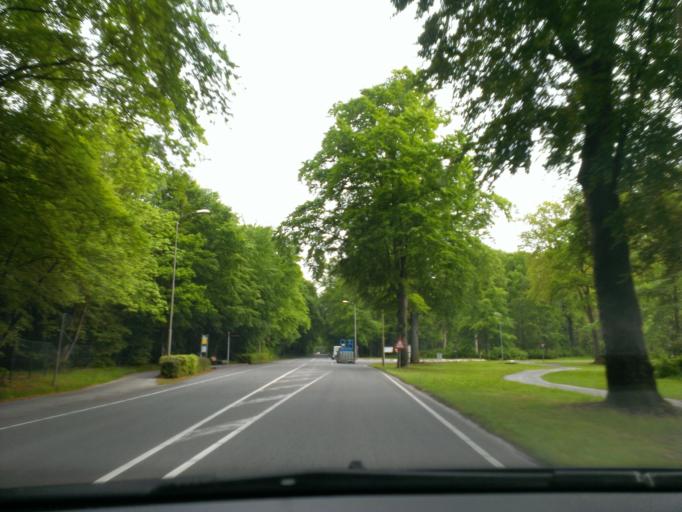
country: NL
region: Gelderland
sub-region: Gemeente Hattem
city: Hattem
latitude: 52.4482
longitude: 6.0697
